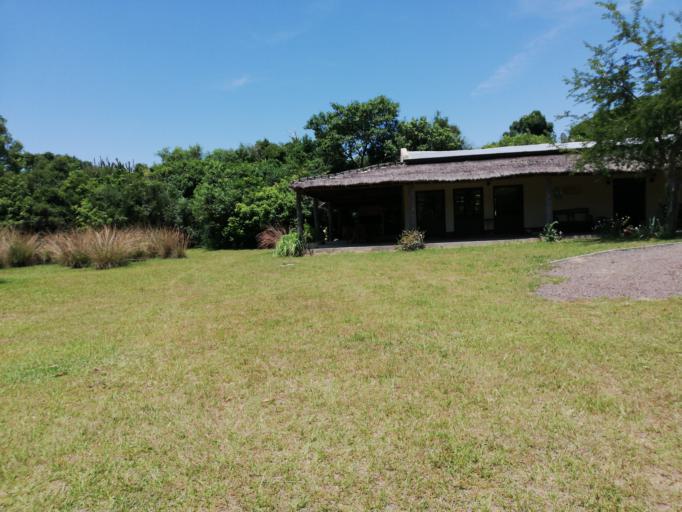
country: AR
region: Corrientes
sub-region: Departamento de San Miguel
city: San Miguel
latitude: -27.9882
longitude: -57.5402
